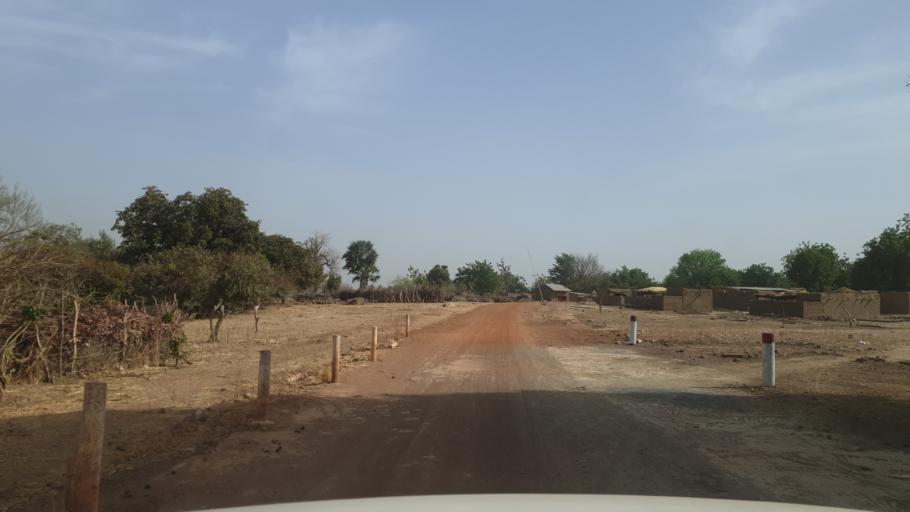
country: ML
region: Koulikoro
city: Kolokani
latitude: 13.3185
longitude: -8.2768
